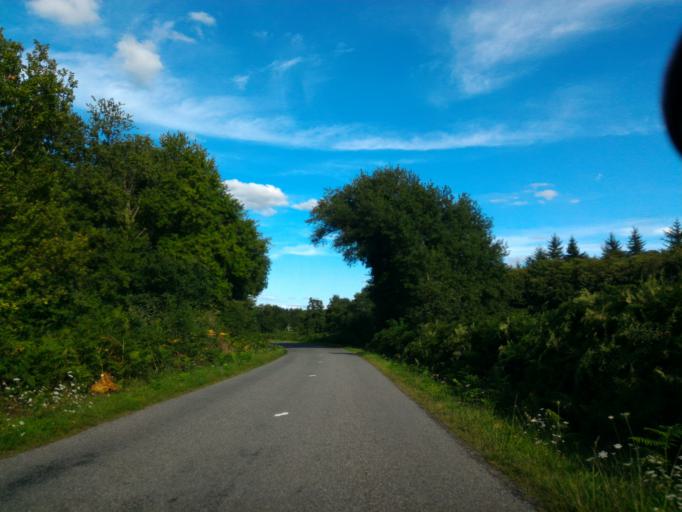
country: FR
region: Poitou-Charentes
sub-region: Departement de la Charente
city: Brigueuil
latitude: 45.9890
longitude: 0.8890
